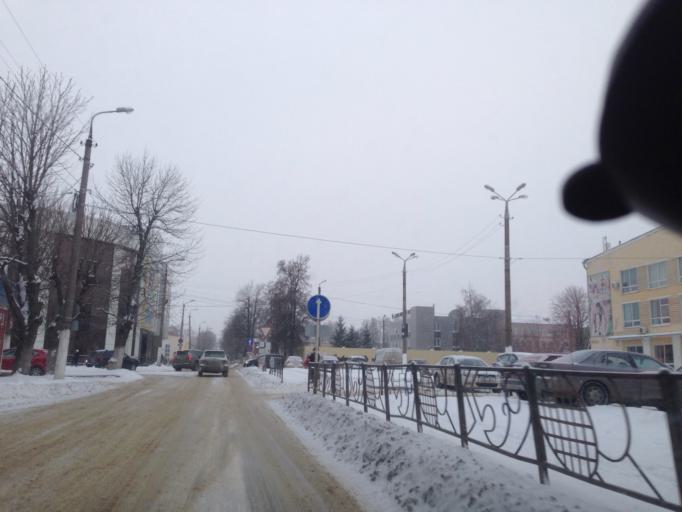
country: RU
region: Tula
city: Novomoskovsk
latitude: 54.0167
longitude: 38.2852
